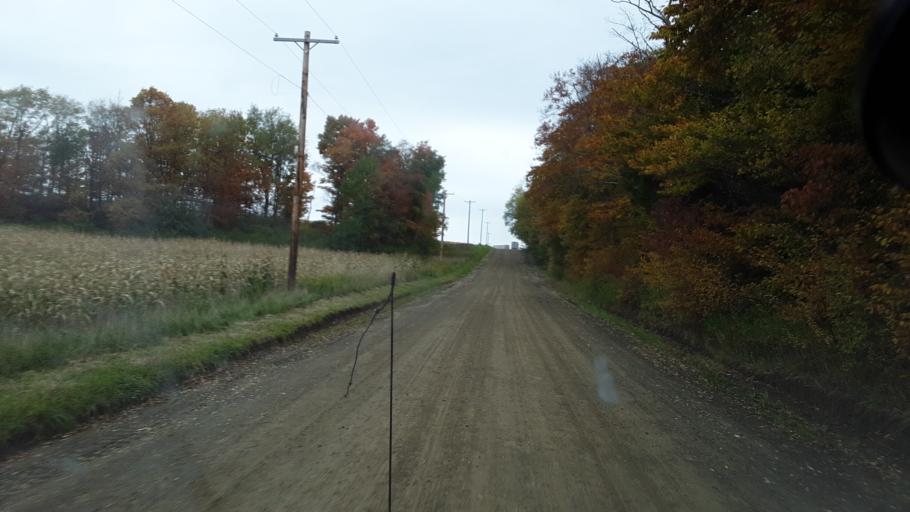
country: US
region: New York
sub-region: Allegany County
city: Andover
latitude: 42.0872
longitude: -77.7960
